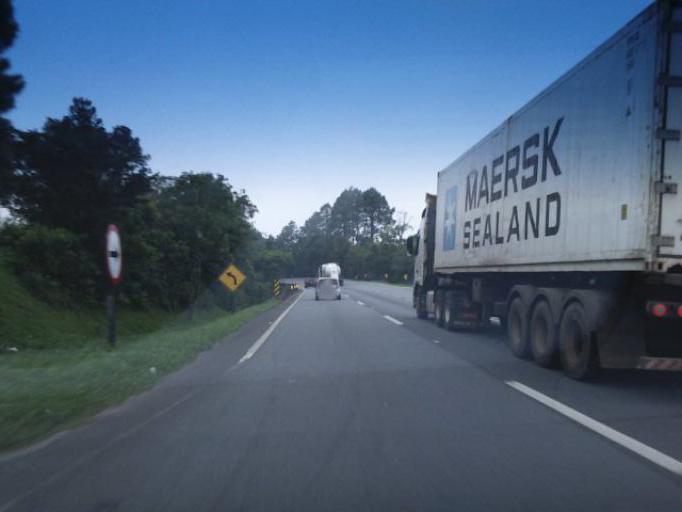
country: BR
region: Parana
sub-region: Sao Jose Dos Pinhais
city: Sao Jose dos Pinhais
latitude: -25.8543
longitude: -49.0256
